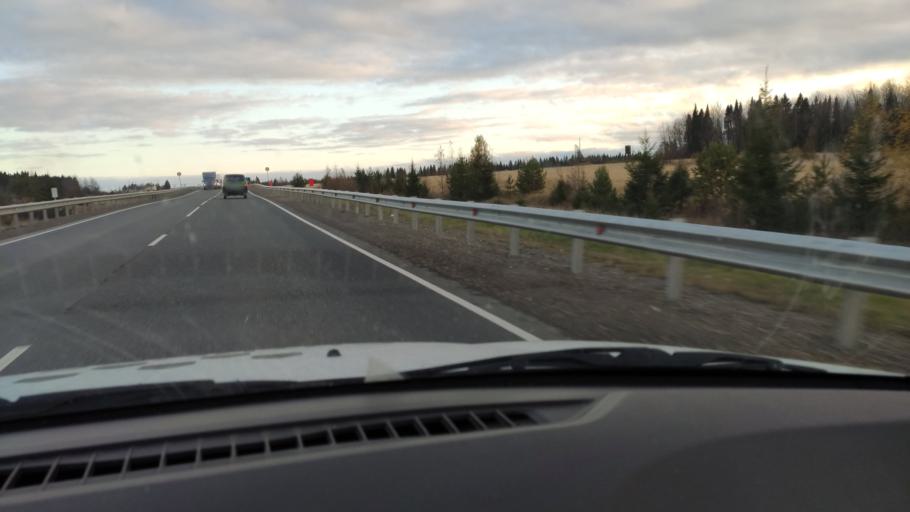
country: RU
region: Kirov
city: Omutninsk
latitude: 58.6900
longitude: 52.1335
